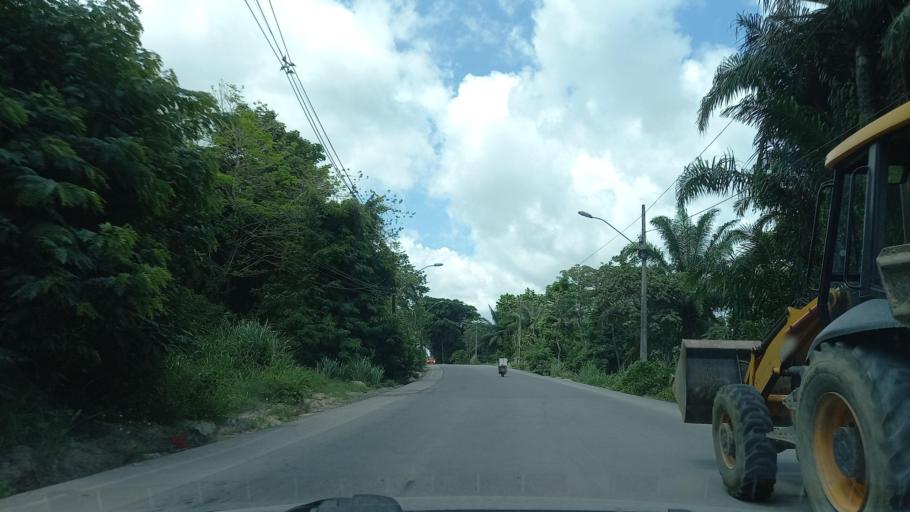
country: BR
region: Pernambuco
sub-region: Jaboatao Dos Guararapes
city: Jaboatao
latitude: -8.1601
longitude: -34.9849
